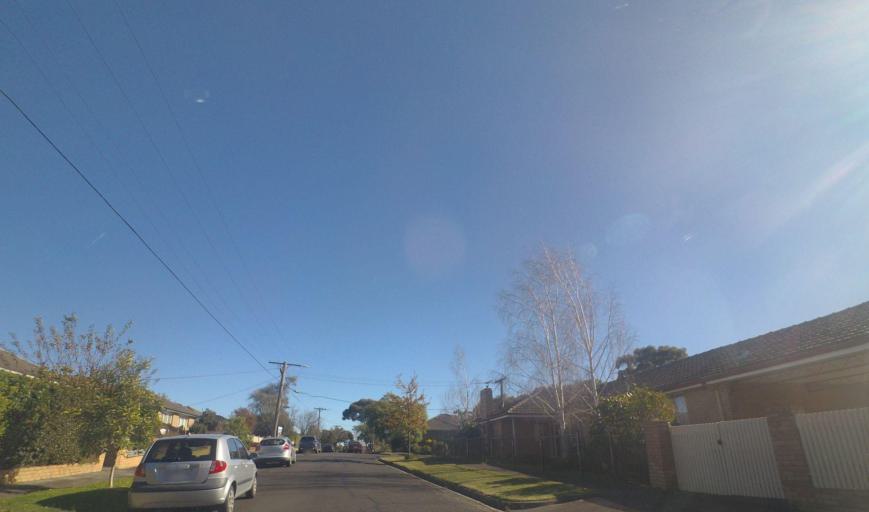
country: AU
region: Victoria
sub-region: Whitehorse
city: Box Hill North
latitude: -37.8048
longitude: 145.1206
